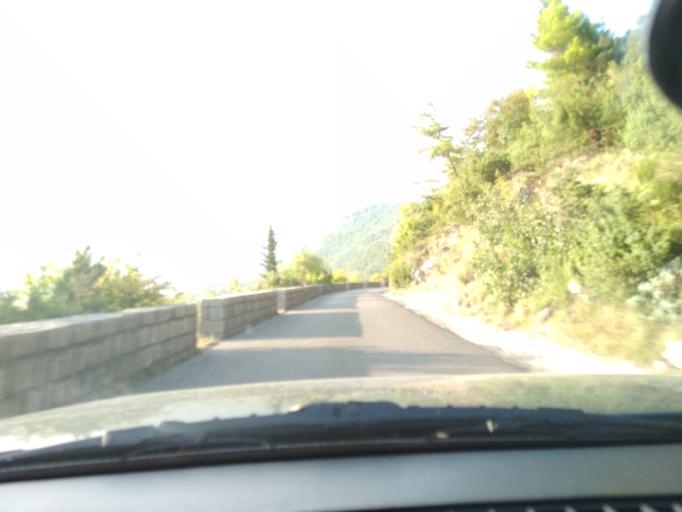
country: ME
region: Kotor
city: Kotor
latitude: 42.3963
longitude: 18.7588
